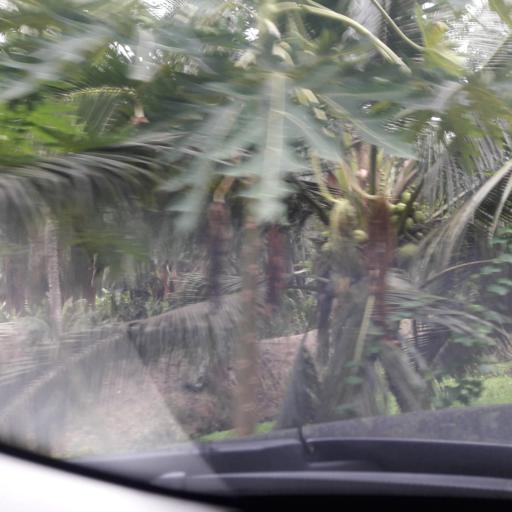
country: TH
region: Ratchaburi
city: Damnoen Saduak
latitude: 13.5777
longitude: 99.9464
